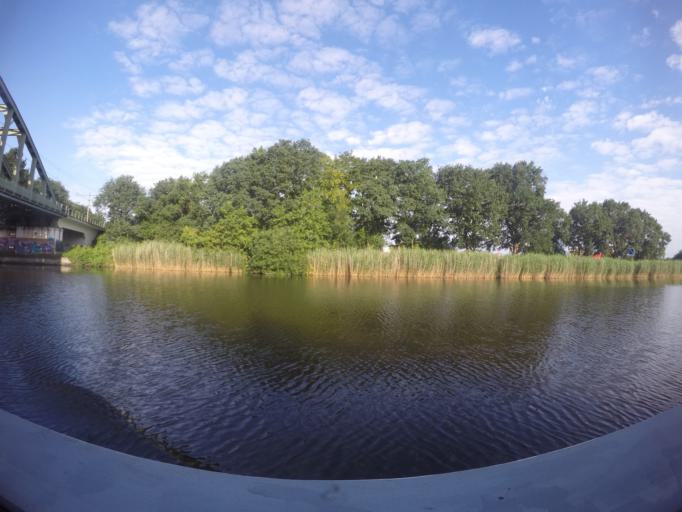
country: NL
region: Overijssel
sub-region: Gemeente Wierden
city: Wierden
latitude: 52.3633
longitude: 6.6216
